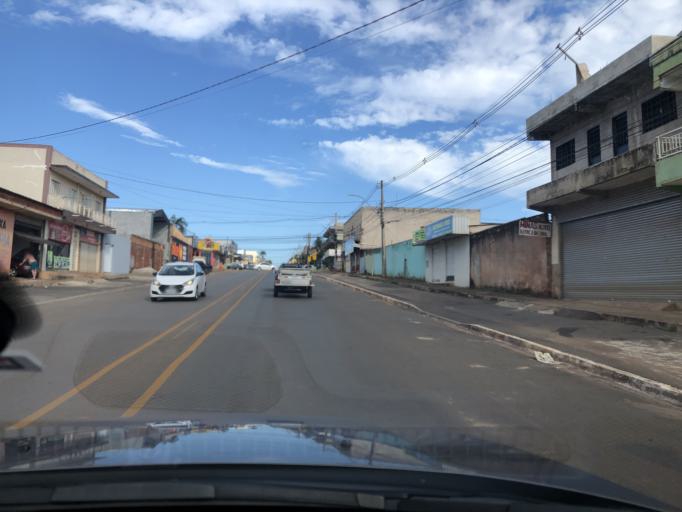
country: BR
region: Federal District
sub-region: Brasilia
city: Brasilia
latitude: -15.7976
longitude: -48.0147
